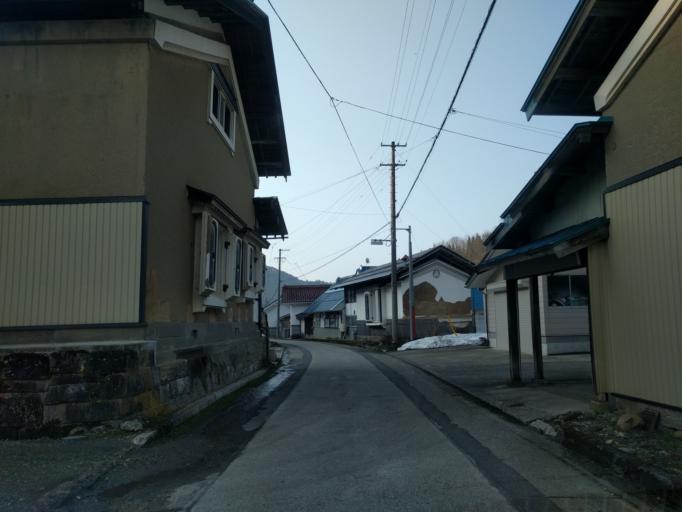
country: JP
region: Fukushima
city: Kitakata
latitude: 37.7061
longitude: 139.9114
